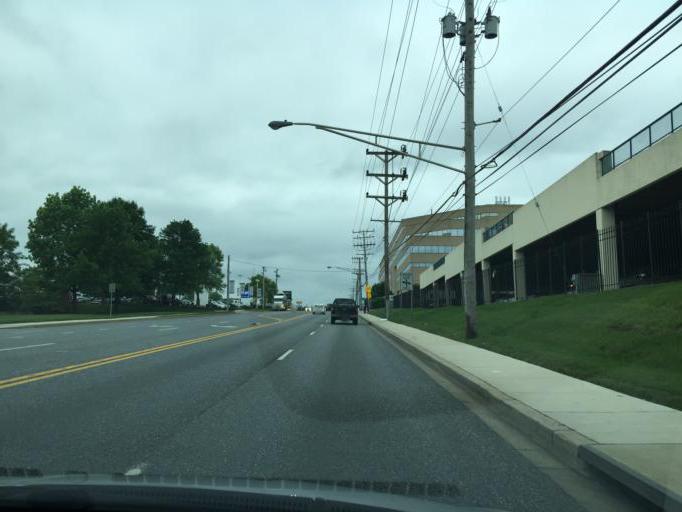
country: US
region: Maryland
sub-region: Baltimore County
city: Cockeysville
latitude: 39.4690
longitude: -76.6386
